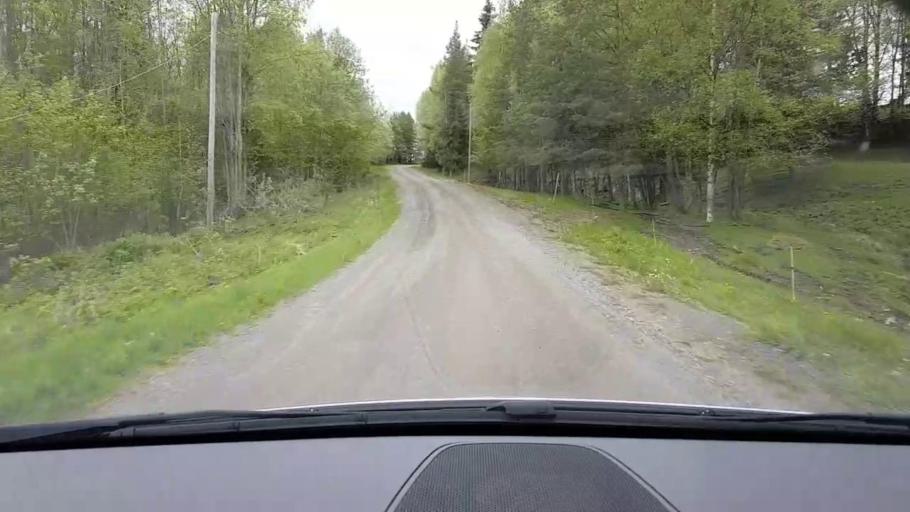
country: SE
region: Jaemtland
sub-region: Bergs Kommun
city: Hoverberg
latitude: 62.8222
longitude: 14.4027
